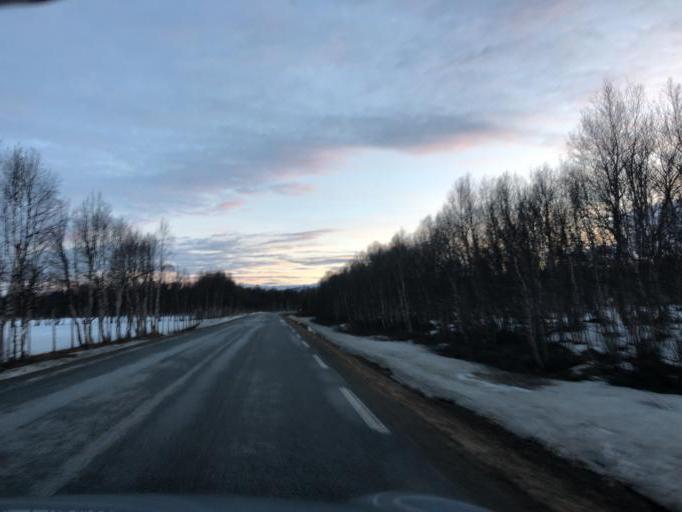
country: NO
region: Sor-Trondelag
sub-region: Tydal
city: Aas
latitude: 62.6738
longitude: 11.8323
